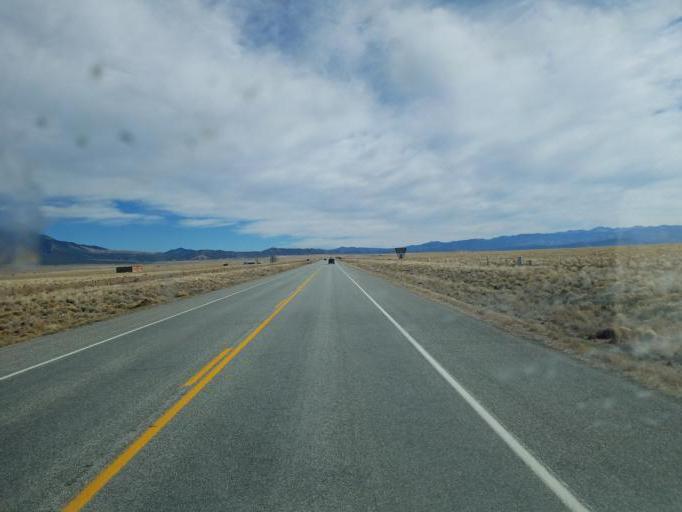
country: US
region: Colorado
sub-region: Alamosa County
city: Alamosa East
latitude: 37.4750
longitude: -105.6117
